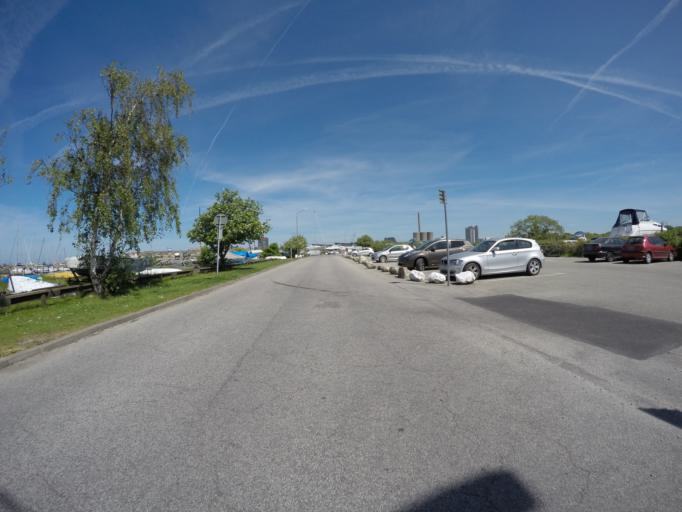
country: SE
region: Skane
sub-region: Malmo
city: Bunkeflostrand
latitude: 55.5833
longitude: 12.9179
